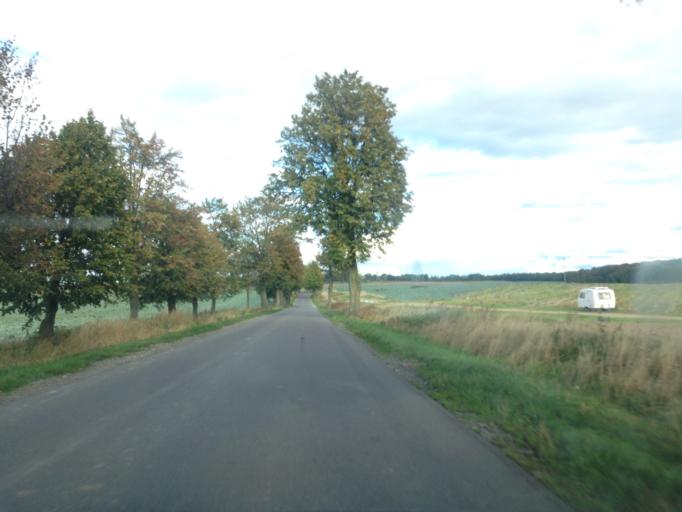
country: PL
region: Warmian-Masurian Voivodeship
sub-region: Powiat ilawski
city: Susz
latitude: 53.6810
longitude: 19.2868
